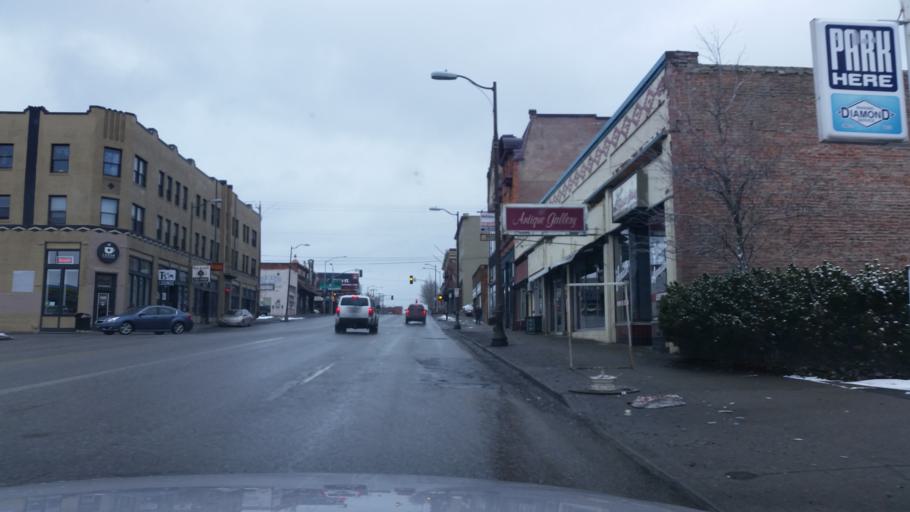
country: US
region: Washington
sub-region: Spokane County
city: Spokane
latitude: 47.6632
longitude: -117.4265
